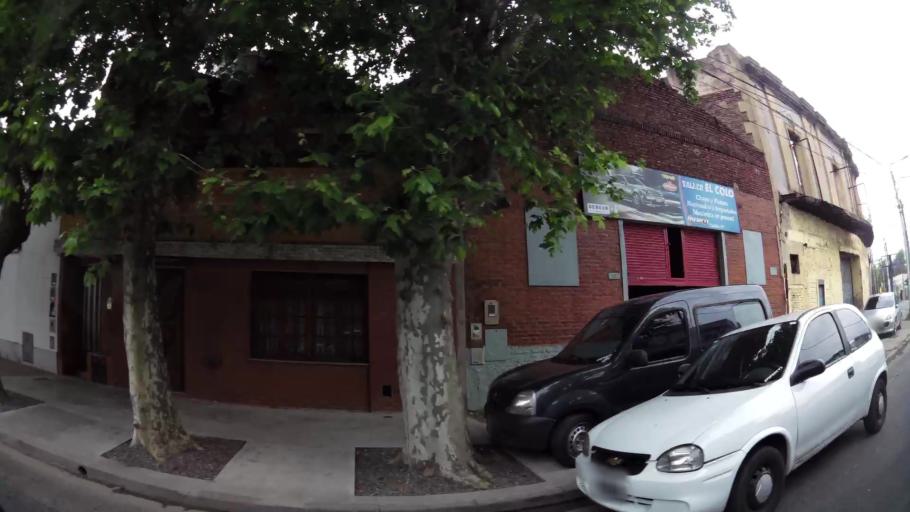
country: AR
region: Buenos Aires
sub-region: Partido de Lanus
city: Lanus
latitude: -34.6741
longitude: -58.3942
